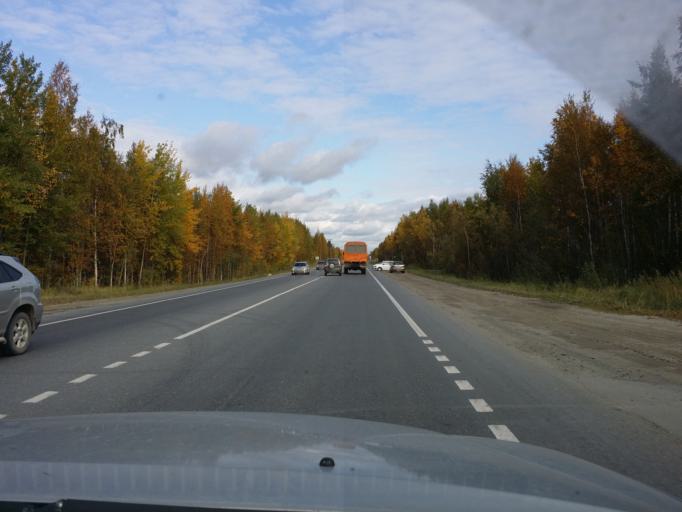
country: RU
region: Khanty-Mansiyskiy Avtonomnyy Okrug
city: Megion
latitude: 61.0637
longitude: 76.1151
